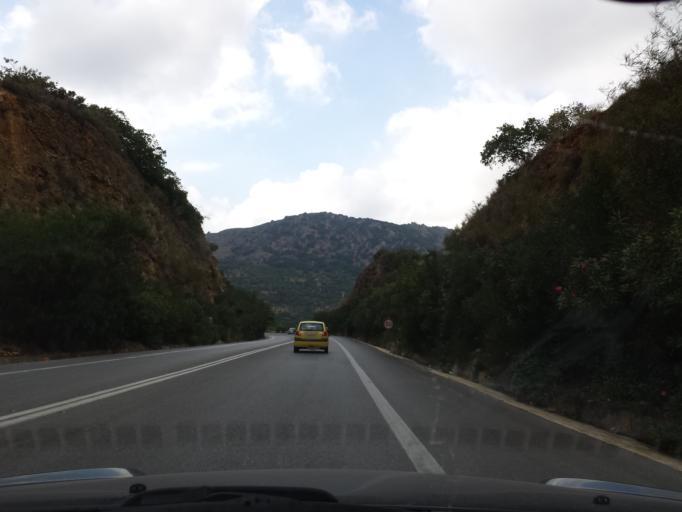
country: GR
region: Crete
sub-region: Nomos Lasithiou
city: Neapoli
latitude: 35.2667
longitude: 25.5806
